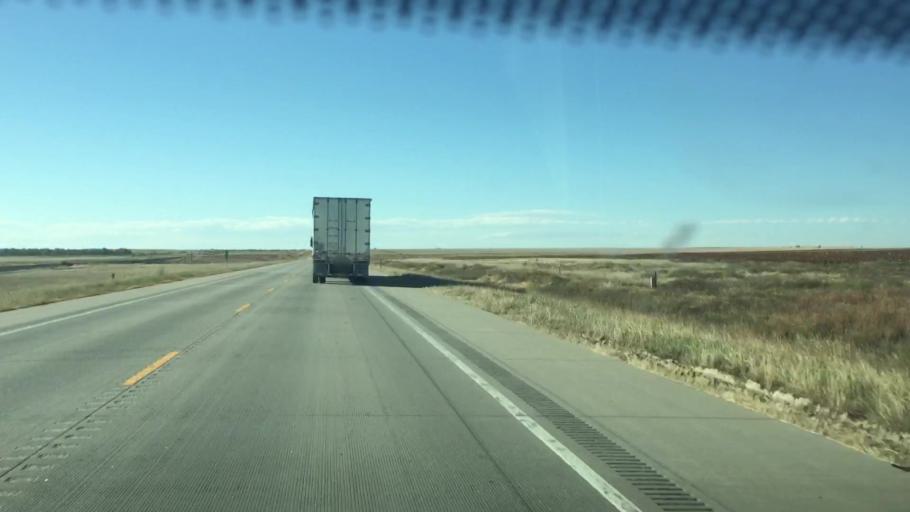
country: US
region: Colorado
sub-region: Kiowa County
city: Eads
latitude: 38.7999
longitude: -102.9555
